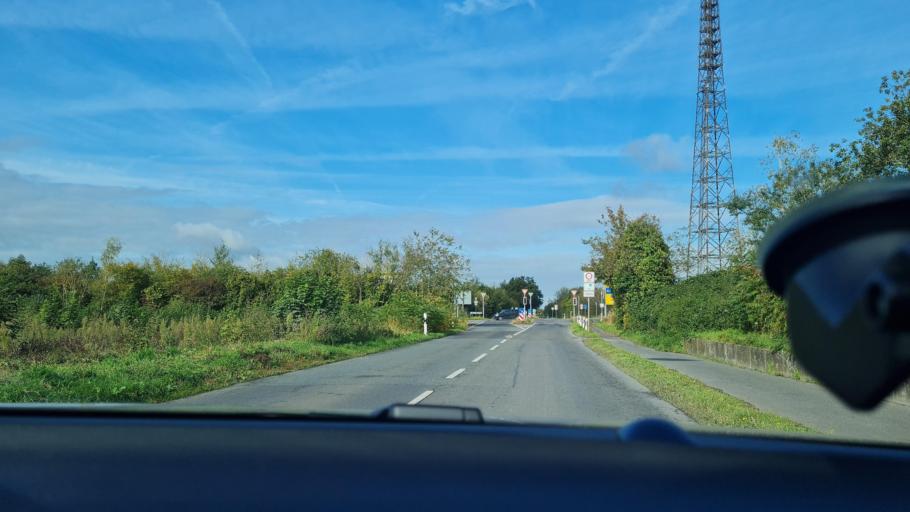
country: DE
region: North Rhine-Westphalia
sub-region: Regierungsbezirk Dusseldorf
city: Dinslaken
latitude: 51.5422
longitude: 6.7533
